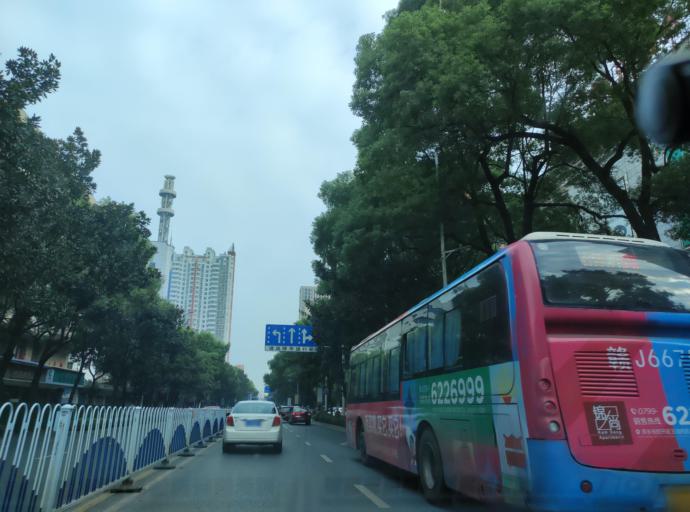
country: CN
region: Jiangxi Sheng
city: Pingxiang
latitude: 27.6423
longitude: 113.8409
